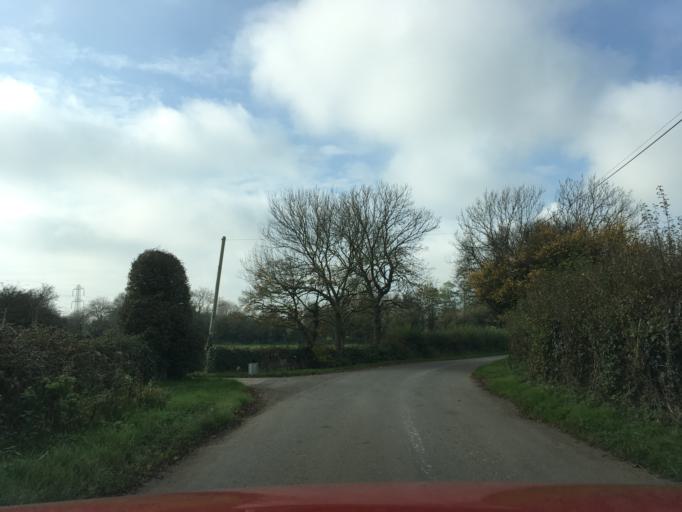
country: GB
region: England
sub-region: South Gloucestershire
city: Wickwar
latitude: 51.5682
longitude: -2.4021
